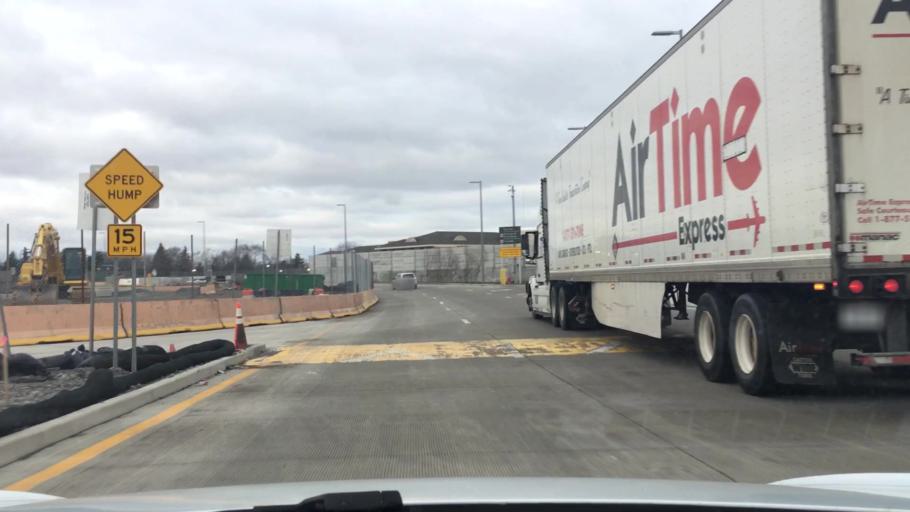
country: US
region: New York
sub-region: Niagara County
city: Lewiston
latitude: 43.1523
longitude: -79.0336
